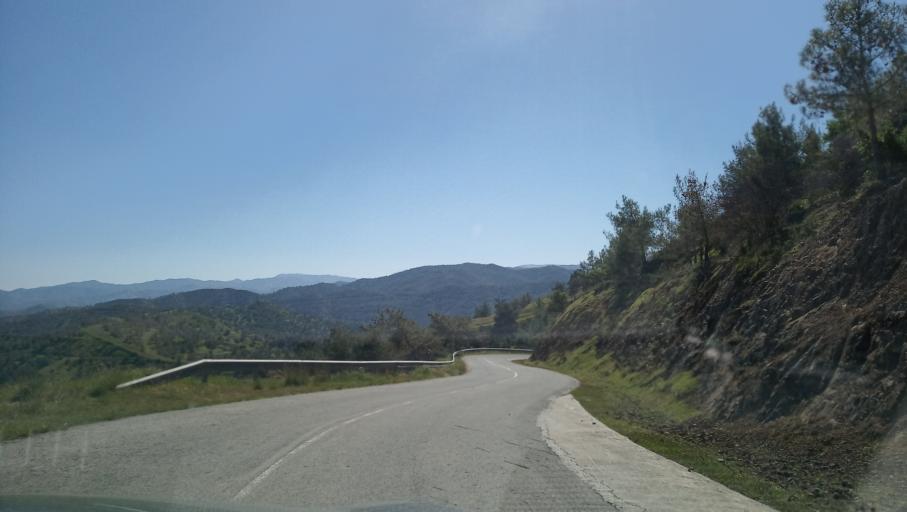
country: CY
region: Lefkosia
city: Lefka
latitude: 35.0919
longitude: 32.7923
